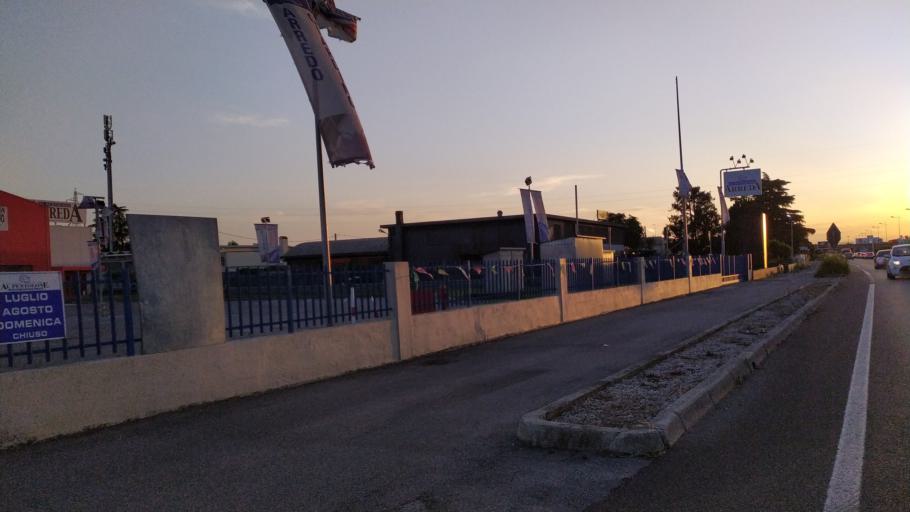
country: IT
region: Veneto
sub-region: Provincia di Padova
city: Vigonza
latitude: 45.4232
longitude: 11.9753
